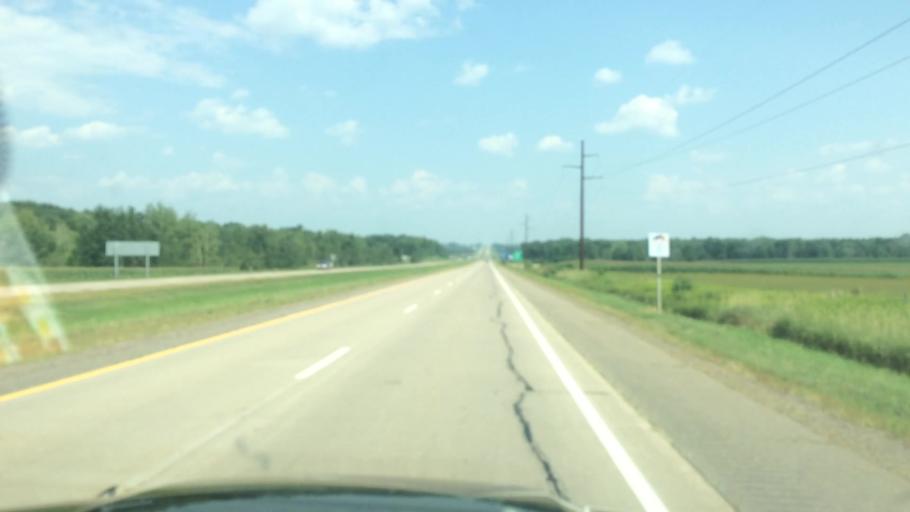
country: US
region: Wisconsin
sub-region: Marathon County
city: Edgar
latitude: 44.9442
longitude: -89.9845
